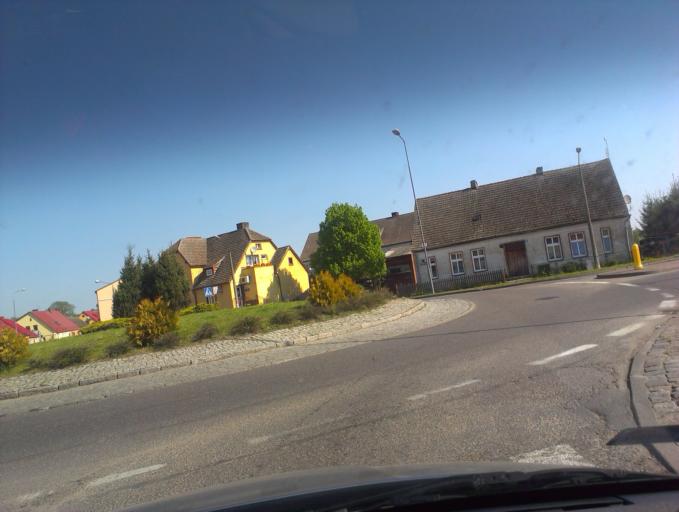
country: PL
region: West Pomeranian Voivodeship
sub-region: Powiat szczecinecki
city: Barwice
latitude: 53.7377
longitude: 16.3546
